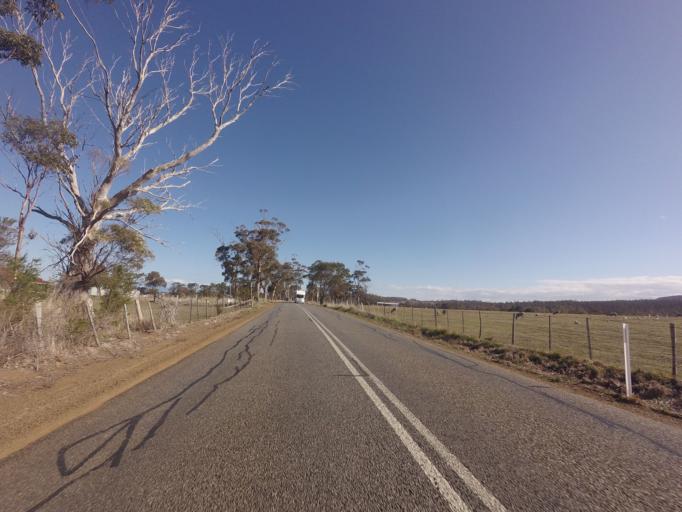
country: AU
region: Tasmania
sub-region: Sorell
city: Sorell
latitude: -42.2542
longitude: 148.0058
